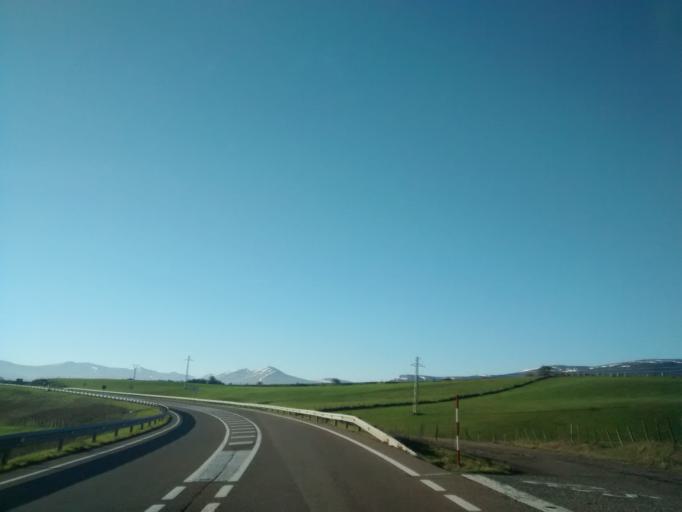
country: ES
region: Cantabria
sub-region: Provincia de Cantabria
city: Reinosa
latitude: 43.0059
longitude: -4.0936
